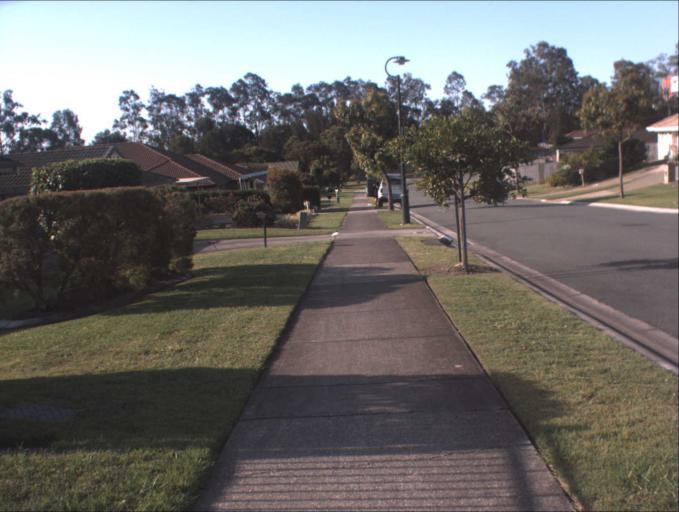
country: AU
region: Queensland
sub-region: Logan
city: Waterford West
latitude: -27.7064
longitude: 153.1547
